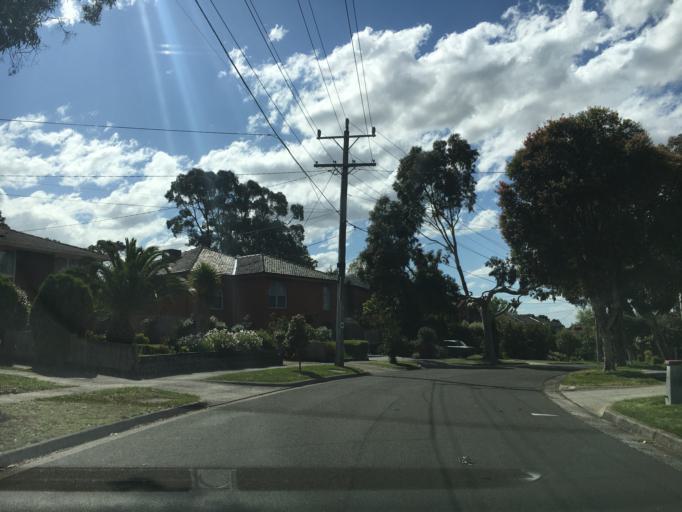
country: AU
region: Victoria
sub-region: Monash
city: Mulgrave
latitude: -37.8933
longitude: 145.1851
